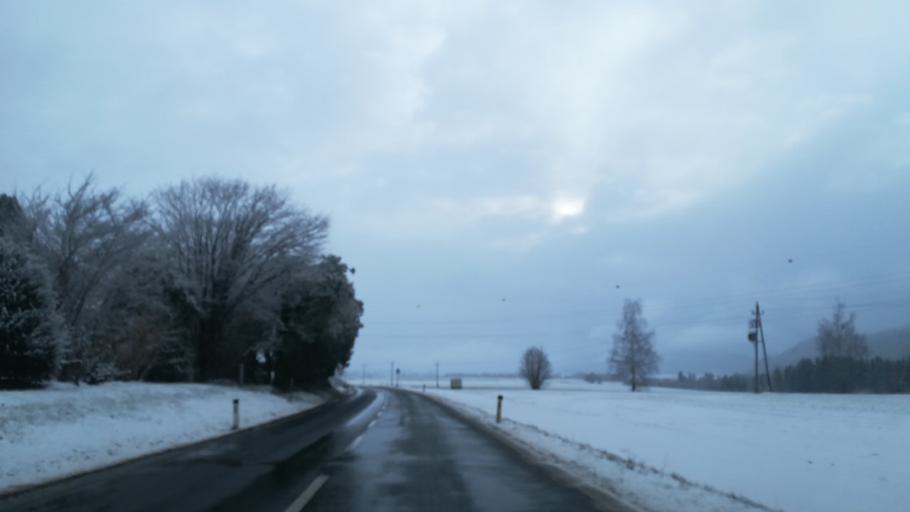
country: AT
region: Styria
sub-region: Politischer Bezirk Murtal
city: Poels
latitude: 47.2076
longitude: 14.6303
